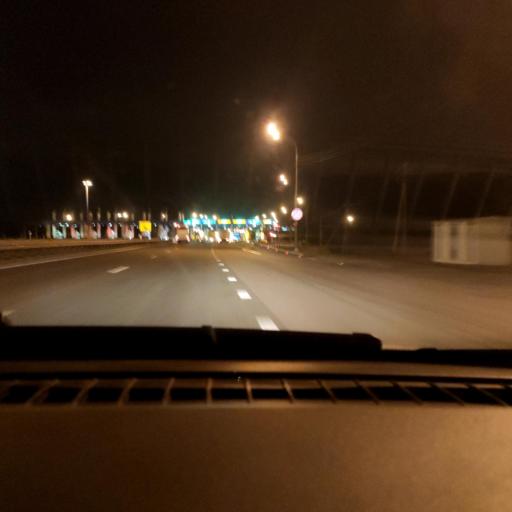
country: RU
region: Lipetsk
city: Khlevnoye
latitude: 52.1272
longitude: 39.1961
